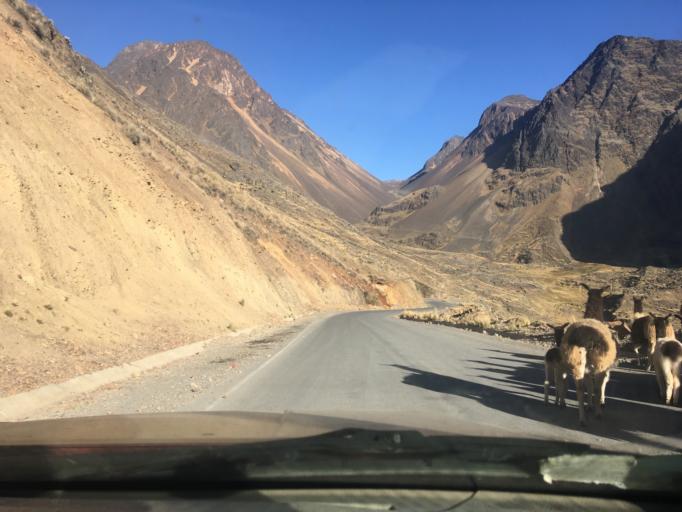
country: BO
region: La Paz
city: Quime
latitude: -17.0280
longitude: -67.2886
